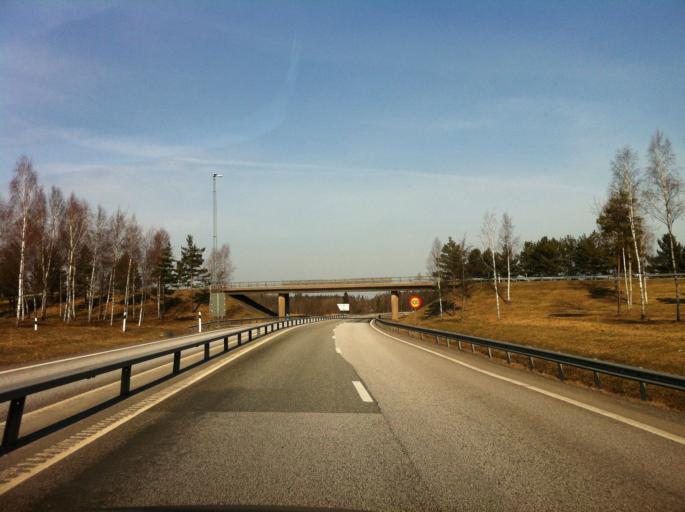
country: SE
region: Joenkoeping
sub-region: Jonkopings Kommun
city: Bankeryd
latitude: 57.8279
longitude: 14.1008
